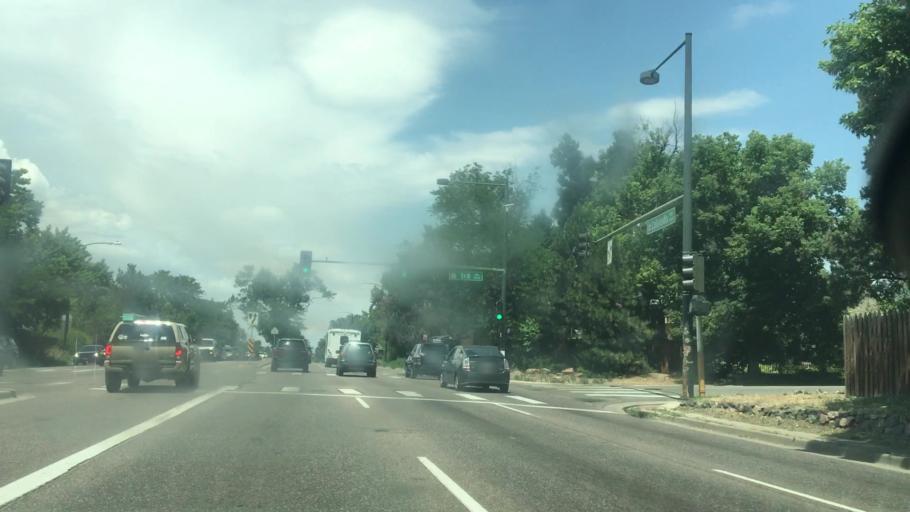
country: US
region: Colorado
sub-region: Arapahoe County
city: Glendale
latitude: 39.7207
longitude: -104.9407
